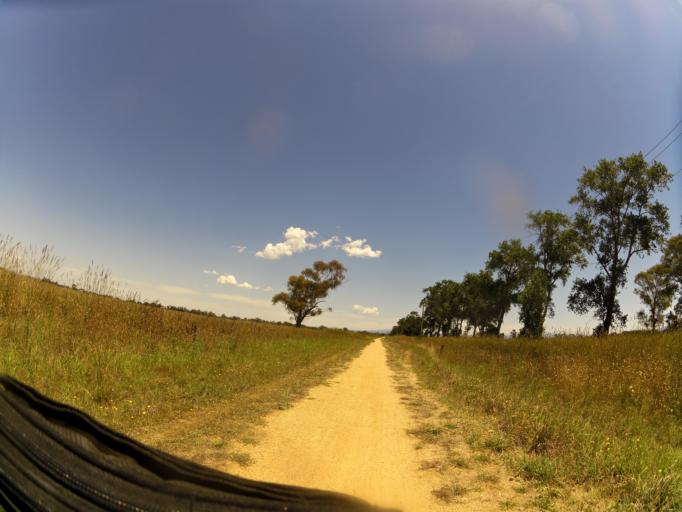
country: AU
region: Victoria
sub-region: Wellington
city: Heyfield
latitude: -37.9683
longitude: 146.9384
